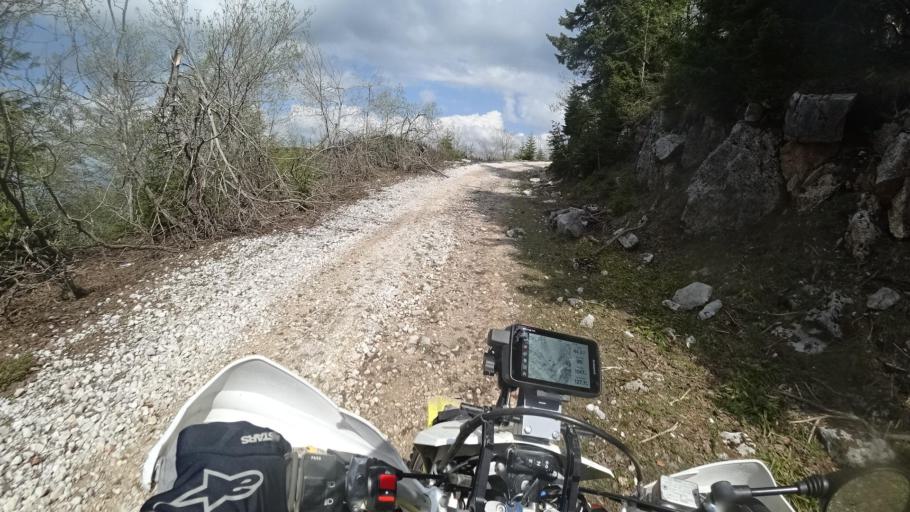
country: BA
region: Republika Srpska
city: Sipovo
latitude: 44.1279
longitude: 17.0435
